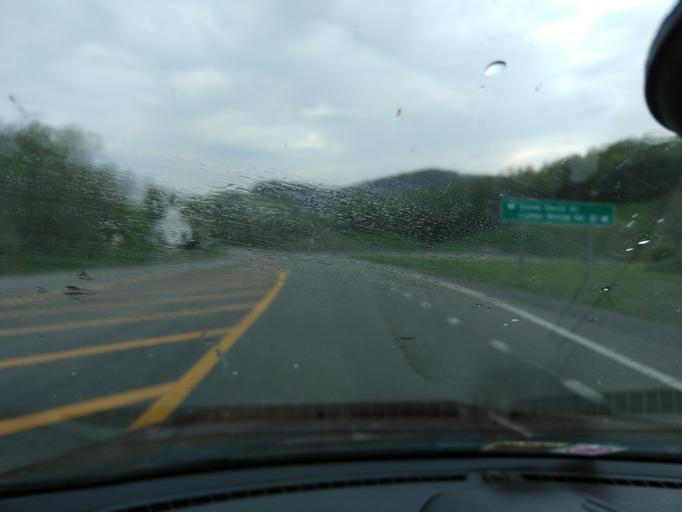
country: US
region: West Virginia
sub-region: Harrison County
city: Despard
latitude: 39.3277
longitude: -80.2883
